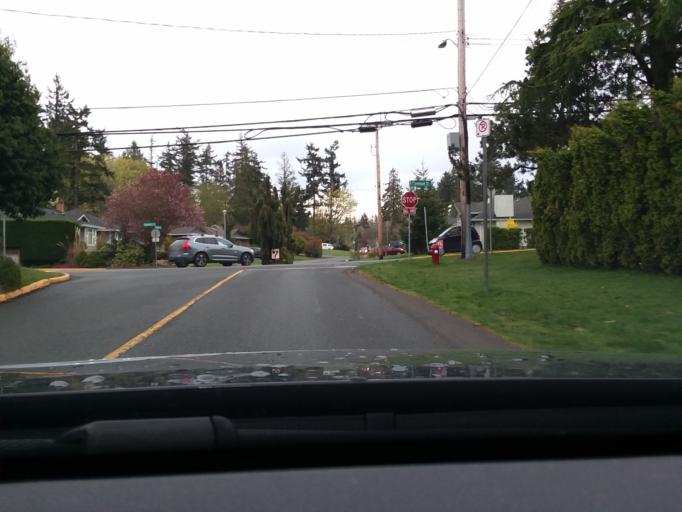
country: CA
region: British Columbia
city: Victoria
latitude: 48.5182
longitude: -123.3782
